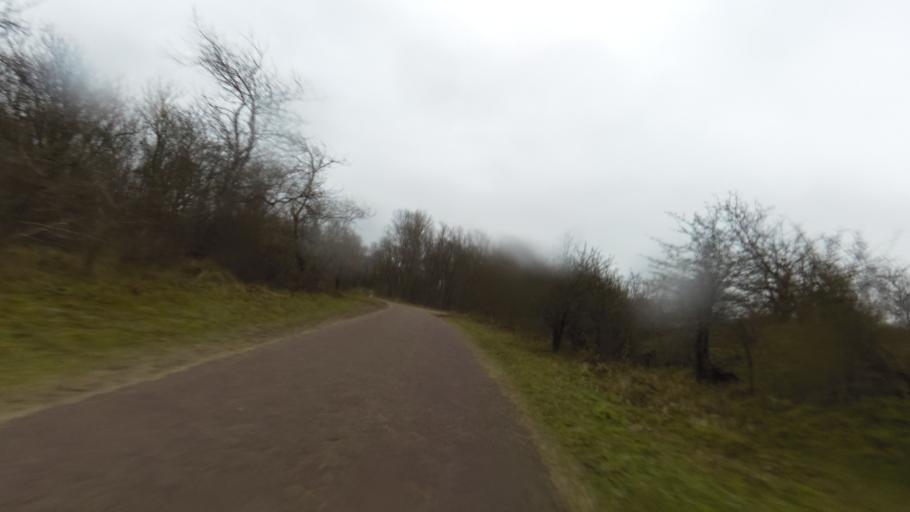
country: NL
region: North Holland
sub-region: Gemeente Bergen
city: Egmond aan Zee
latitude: 52.5766
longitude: 4.6219
